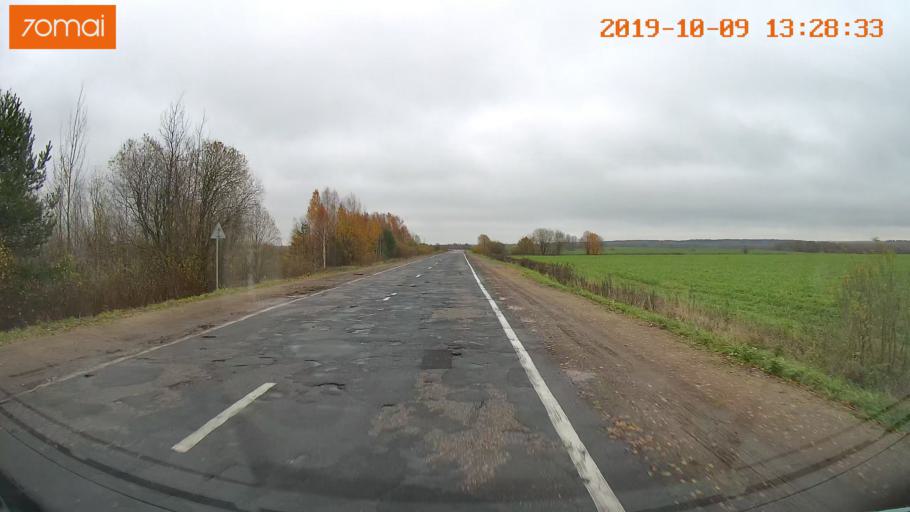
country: RU
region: Jaroslavl
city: Lyubim
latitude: 58.3142
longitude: 40.9706
